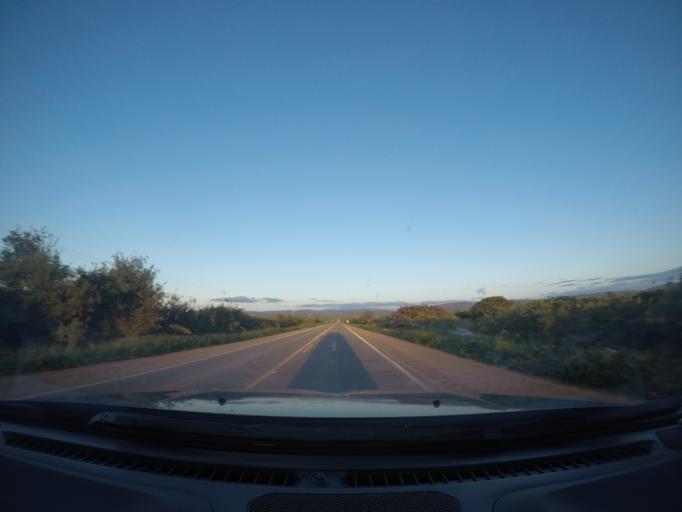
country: BR
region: Bahia
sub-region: Seabra
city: Seabra
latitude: -12.4035
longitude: -41.9517
